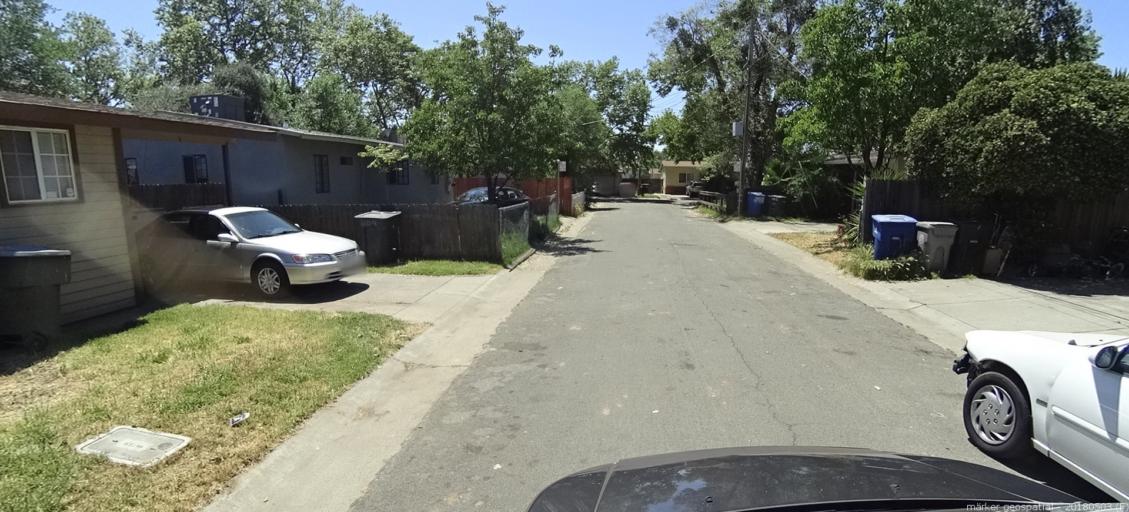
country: US
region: California
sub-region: Sacramento County
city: Rio Linda
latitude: 38.6425
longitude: -121.4246
